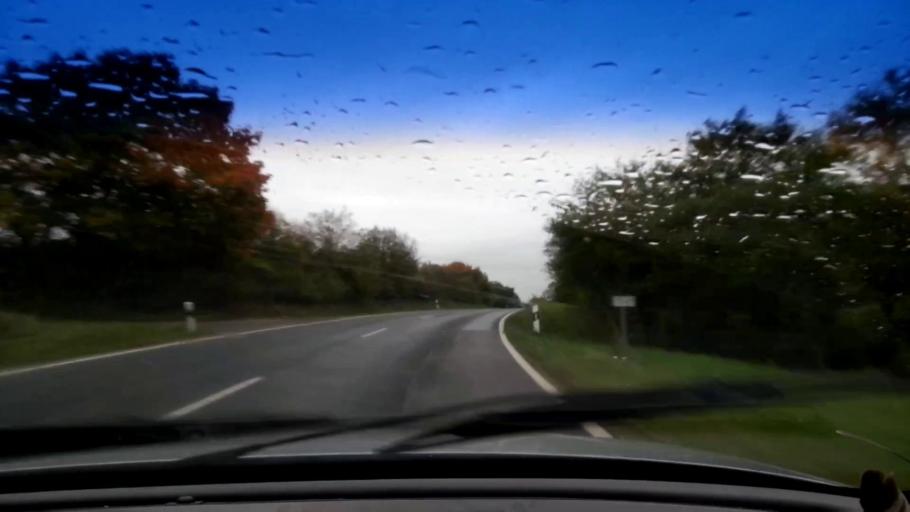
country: DE
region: Bavaria
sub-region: Upper Franconia
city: Priesendorf
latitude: 49.8605
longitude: 10.6815
